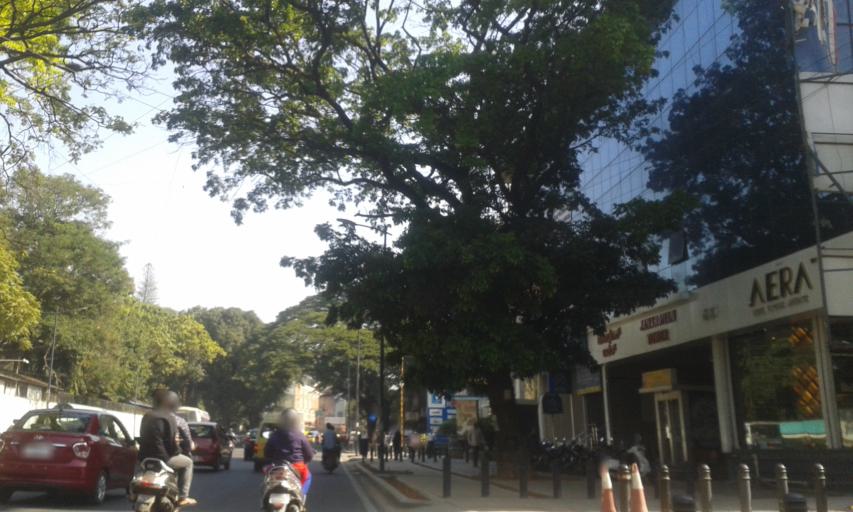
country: IN
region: Karnataka
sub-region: Bangalore Urban
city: Bangalore
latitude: 12.9668
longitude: 77.5990
